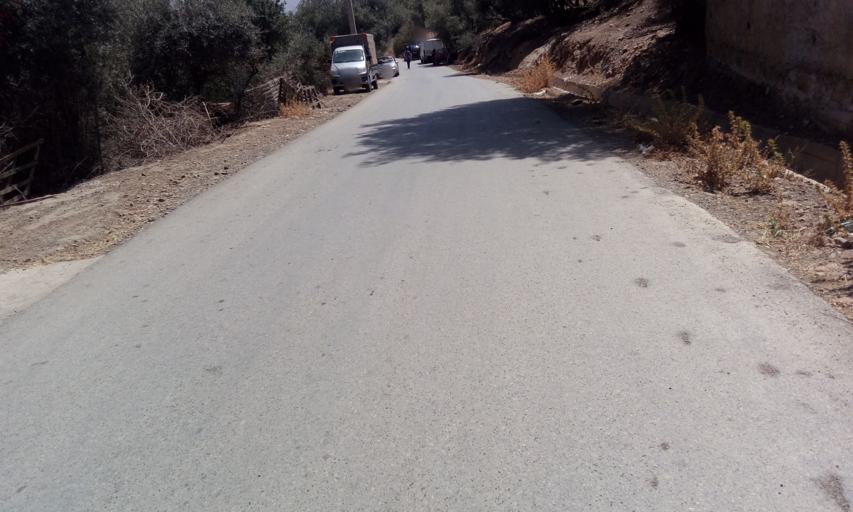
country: DZ
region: Tizi Ouzou
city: Chemini
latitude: 36.6066
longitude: 4.6361
